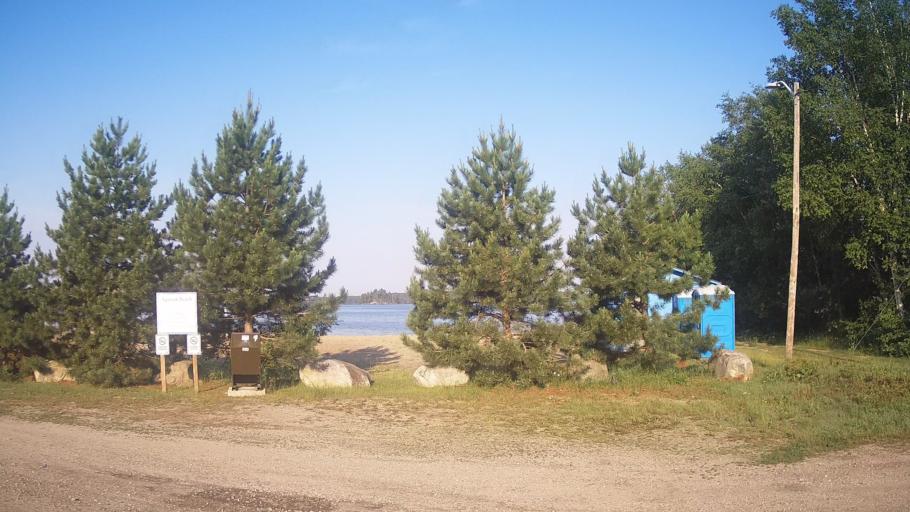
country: CA
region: Ontario
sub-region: Rainy River District
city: Atikokan
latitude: 49.4054
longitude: -91.6667
